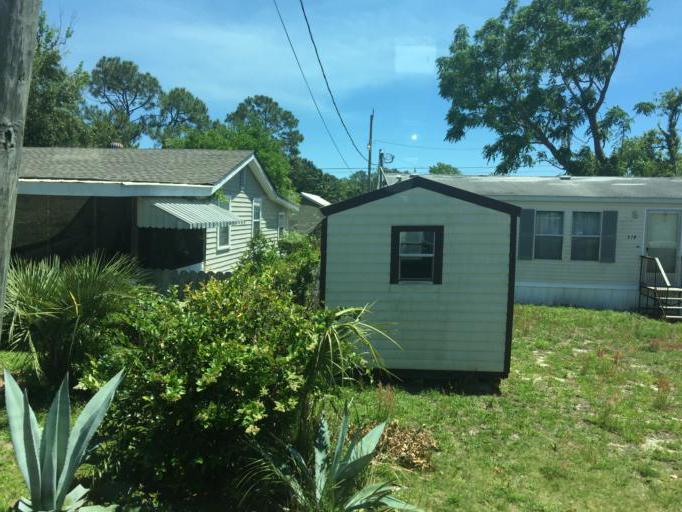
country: US
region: Florida
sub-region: Bay County
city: Laguna Beach
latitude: 30.2417
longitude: -85.9181
